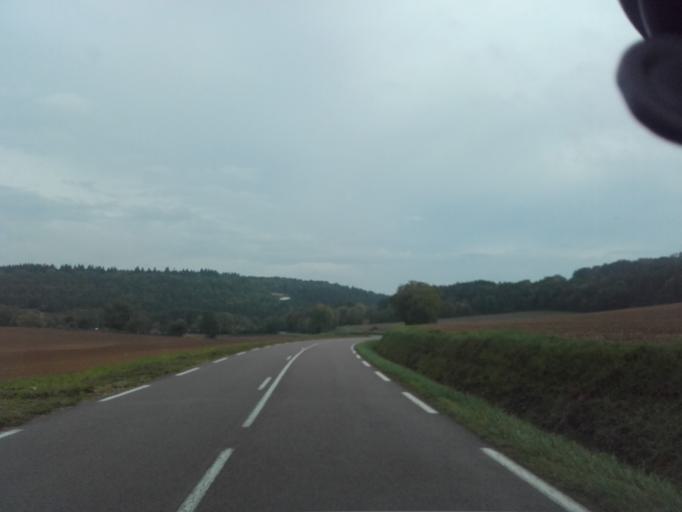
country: FR
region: Bourgogne
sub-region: Departement de la Cote-d'Or
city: Savigny-les-Beaune
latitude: 47.0489
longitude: 4.7873
